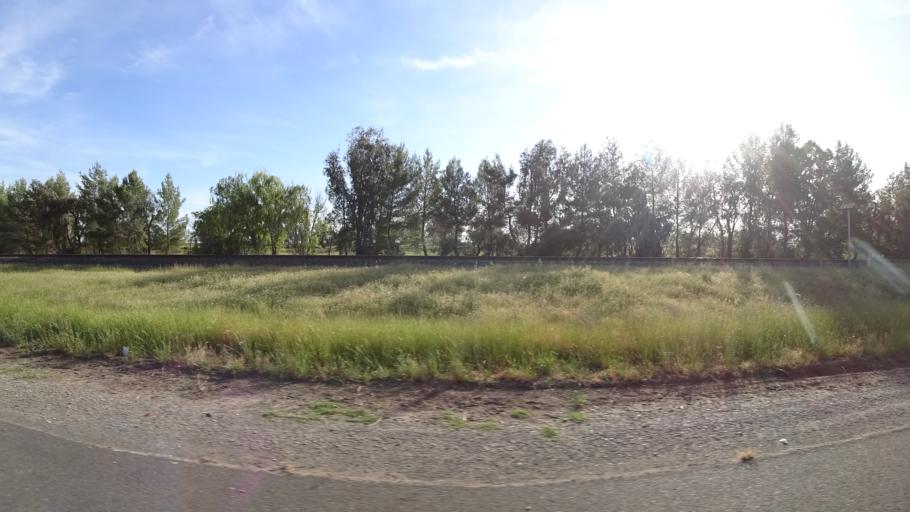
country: US
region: California
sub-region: Placer County
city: Sheridan
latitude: 38.9644
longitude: -121.3625
